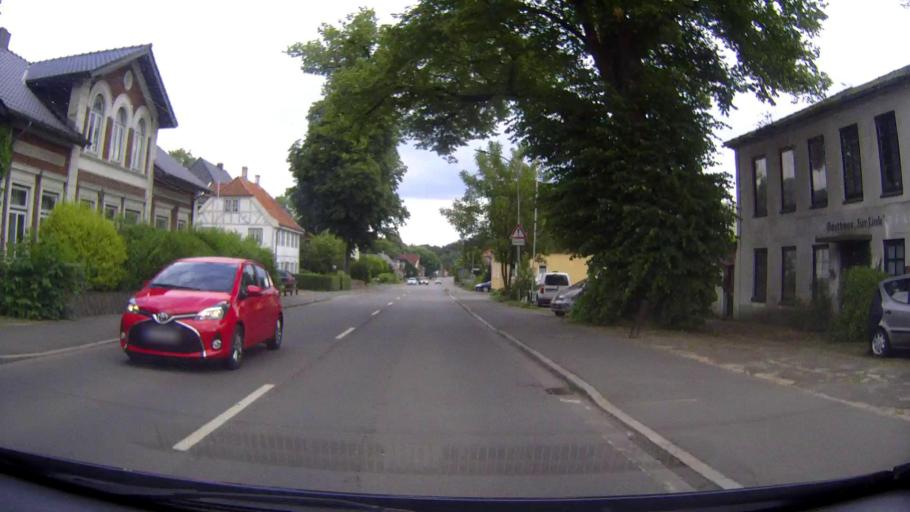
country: DE
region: Schleswig-Holstein
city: Hanerau-Hademarschen
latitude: 54.1206
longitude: 9.4397
